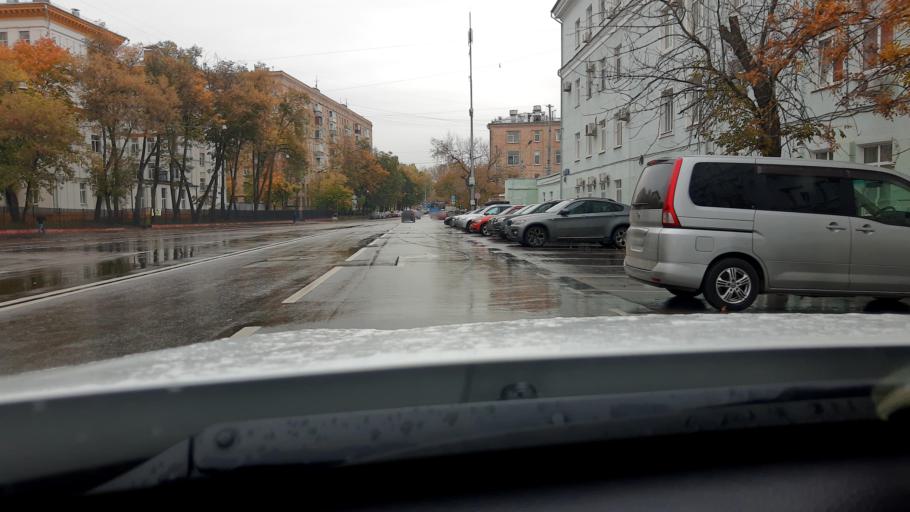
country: RU
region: Moscow
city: Vorob'yovo
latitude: 55.7395
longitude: 37.5194
